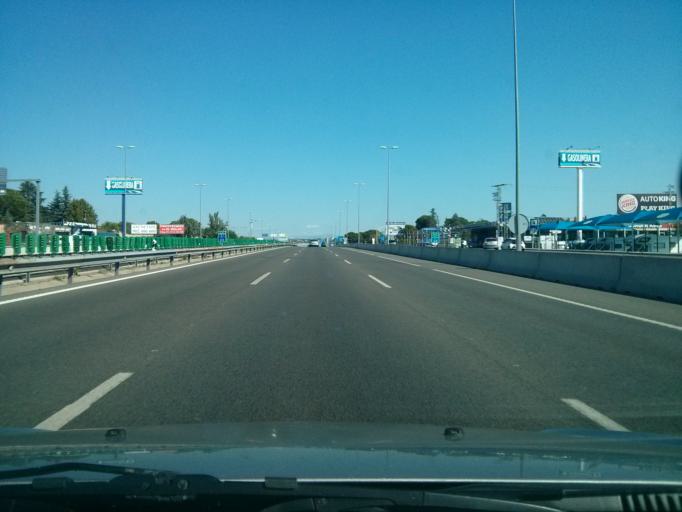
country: ES
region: Madrid
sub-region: Provincia de Madrid
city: San Sebastian de los Reyes
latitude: 40.5892
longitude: -3.5830
